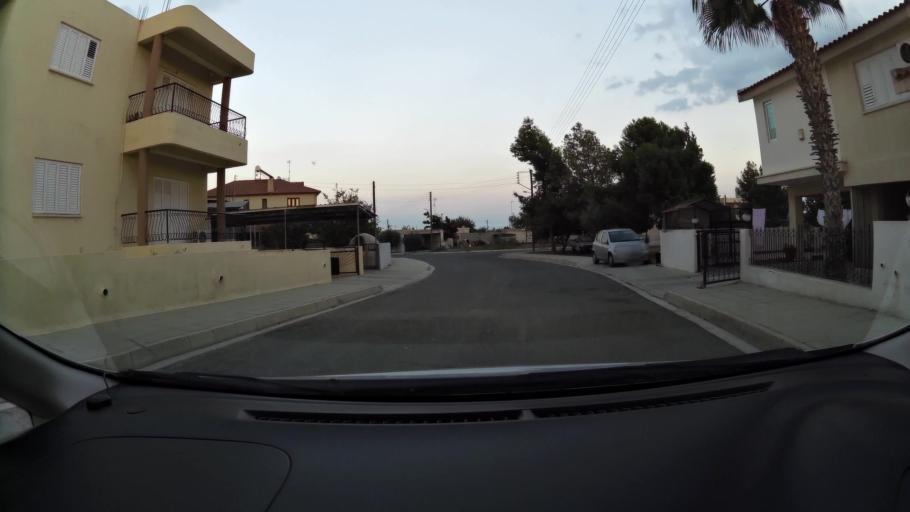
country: CY
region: Larnaka
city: Dhromolaxia
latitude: 34.8792
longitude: 33.5833
